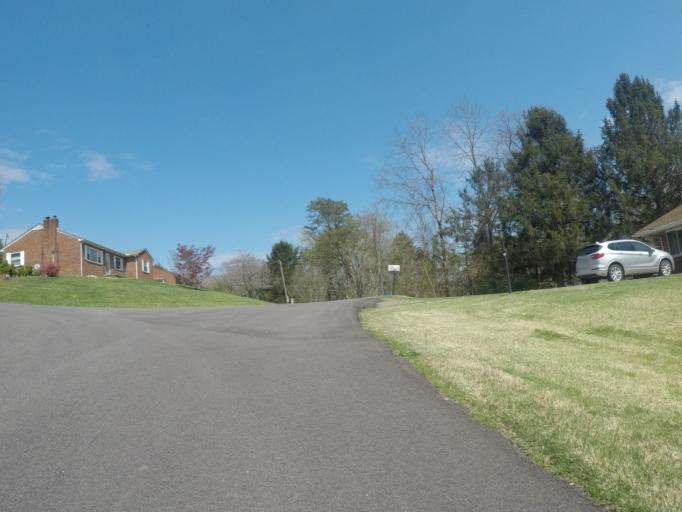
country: US
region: Ohio
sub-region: Lawrence County
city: Burlington
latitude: 38.3803
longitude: -82.5280
